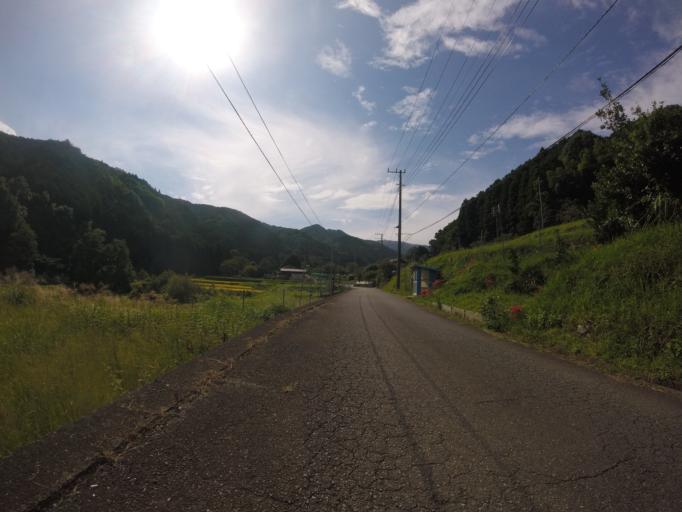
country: JP
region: Shizuoka
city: Heda
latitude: 34.9452
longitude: 138.8853
